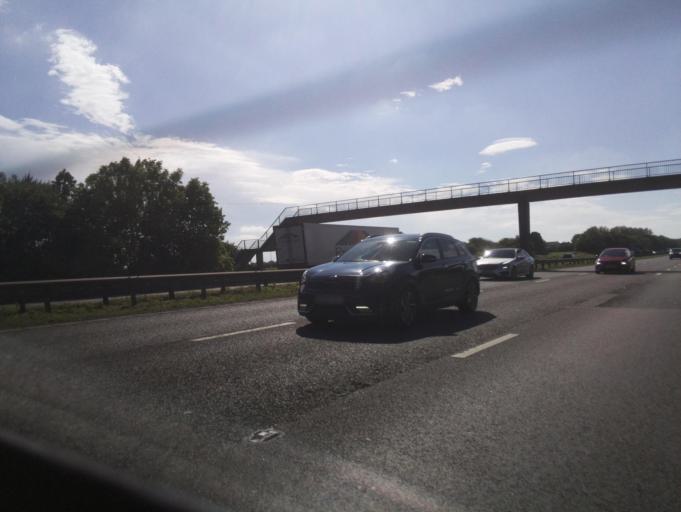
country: GB
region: England
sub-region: Borough of Wigan
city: Tyldesley
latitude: 53.5465
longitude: -2.4566
